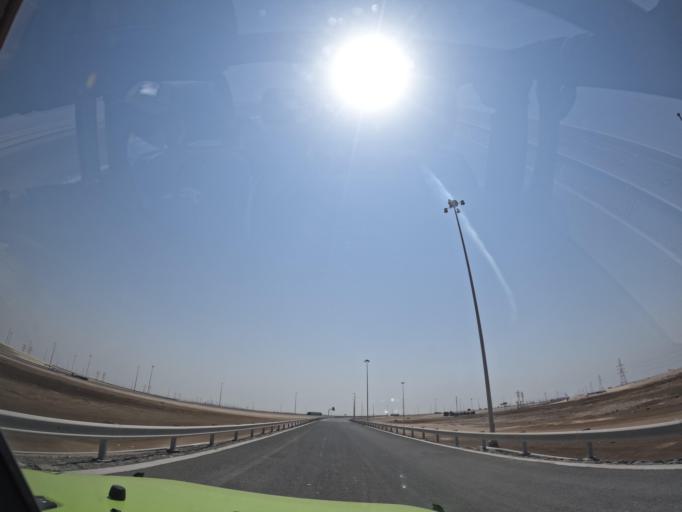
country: AE
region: Abu Dhabi
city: Abu Dhabi
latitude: 24.2146
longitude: 54.4120
